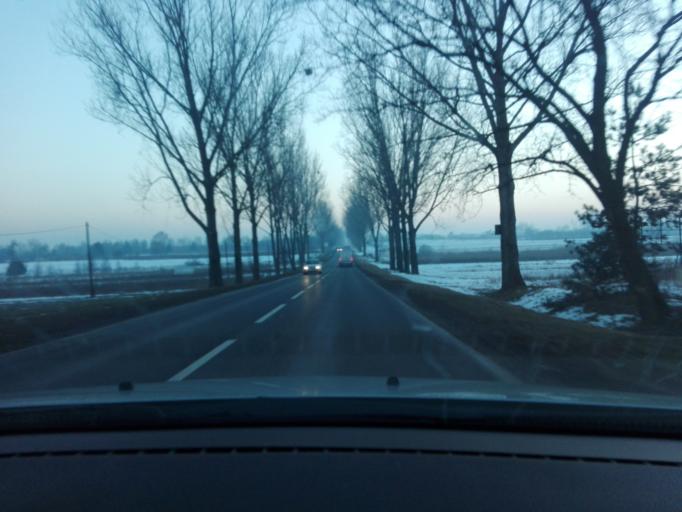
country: PL
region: Lodz Voivodeship
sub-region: Powiat zgierski
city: Zgierz
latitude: 51.9017
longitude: 19.4268
